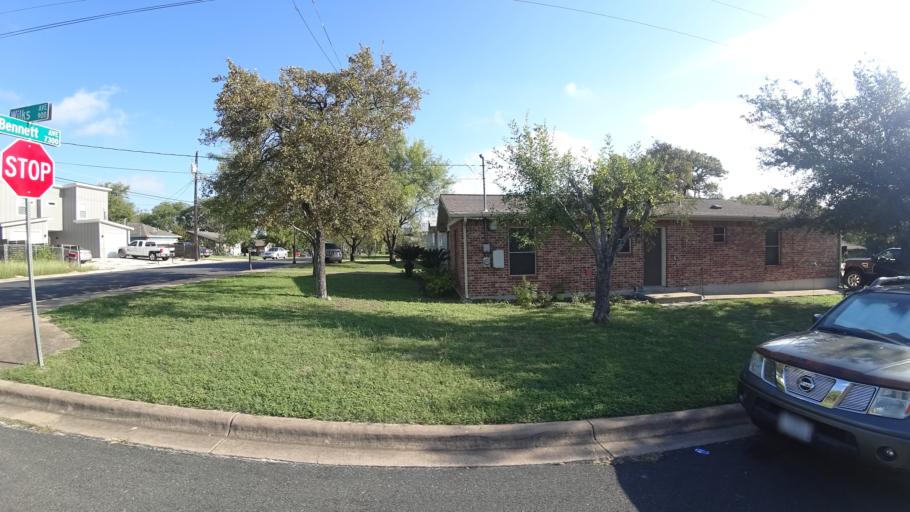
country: US
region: Texas
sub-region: Travis County
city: Austin
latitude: 30.3322
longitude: -97.6995
